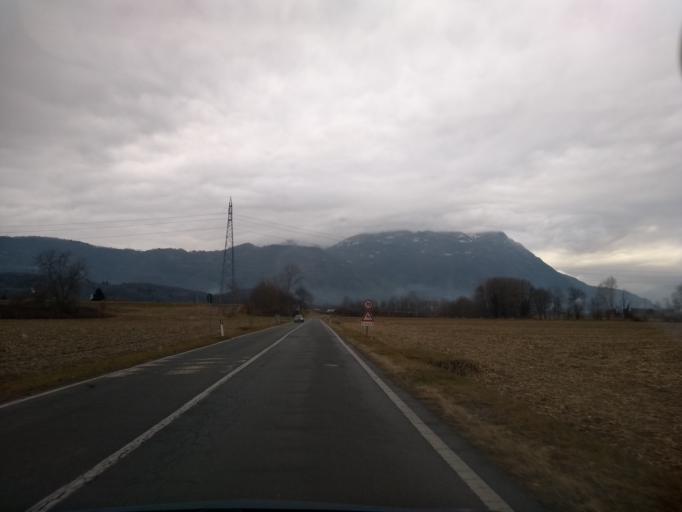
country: IT
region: Piedmont
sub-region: Provincia di Torino
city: Salerano Canavese
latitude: 45.4635
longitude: 7.8466
